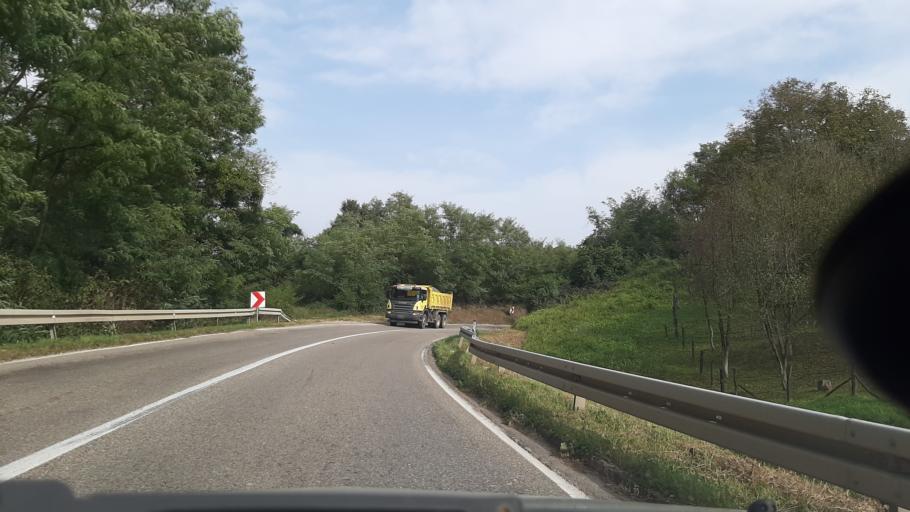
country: BA
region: Republika Srpska
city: Laktasi
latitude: 44.8736
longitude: 17.3571
